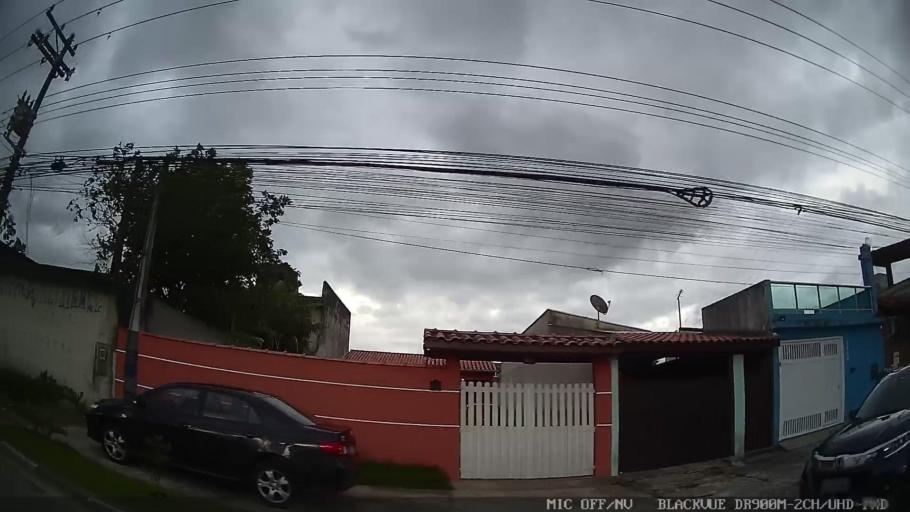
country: BR
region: Sao Paulo
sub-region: Caraguatatuba
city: Caraguatatuba
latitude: -23.6537
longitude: -45.4285
